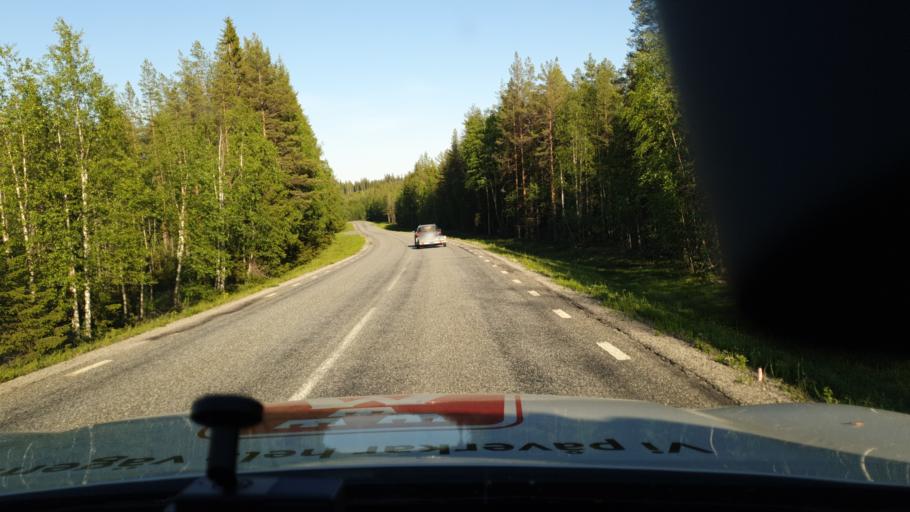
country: SE
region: Vaesterbotten
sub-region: Lycksele Kommun
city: Lycksele
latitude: 64.6229
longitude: 18.3986
